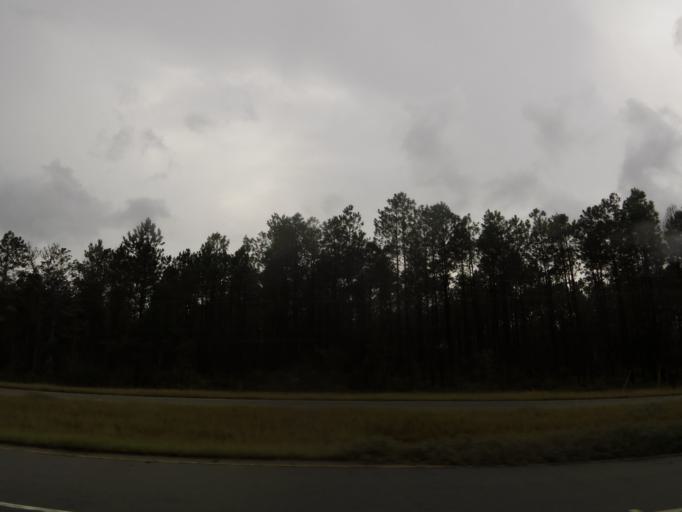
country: US
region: Georgia
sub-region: Wayne County
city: Jesup
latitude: 31.4628
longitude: -81.7118
